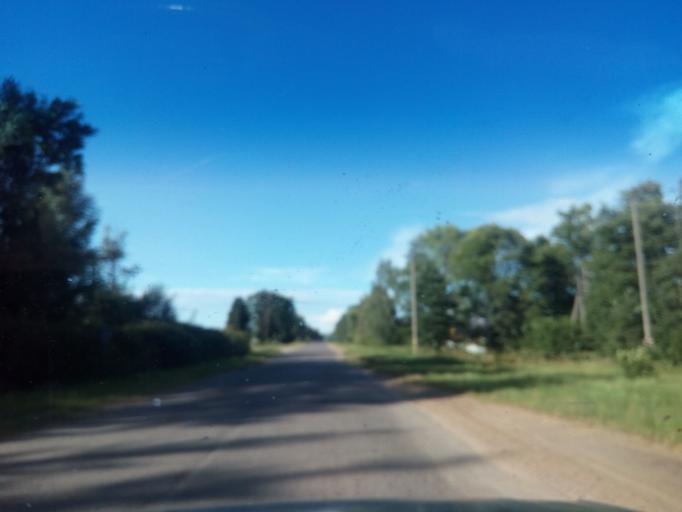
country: BY
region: Vitebsk
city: Dzisna
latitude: 55.6551
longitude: 28.3223
